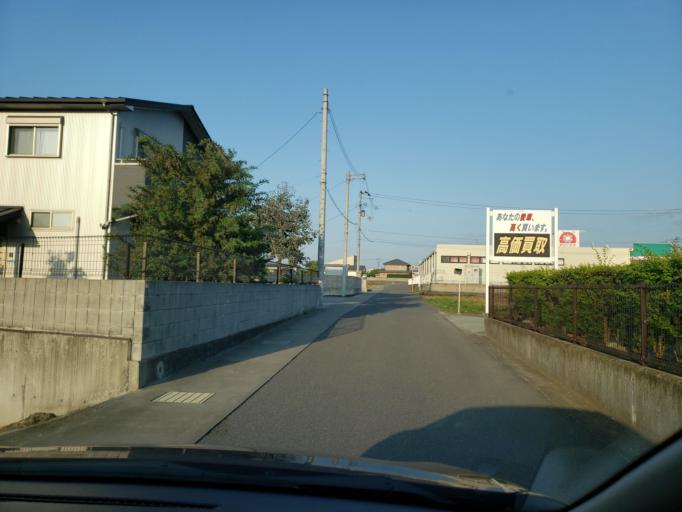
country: JP
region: Tokushima
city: Wakimachi
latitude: 34.0756
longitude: 134.2328
